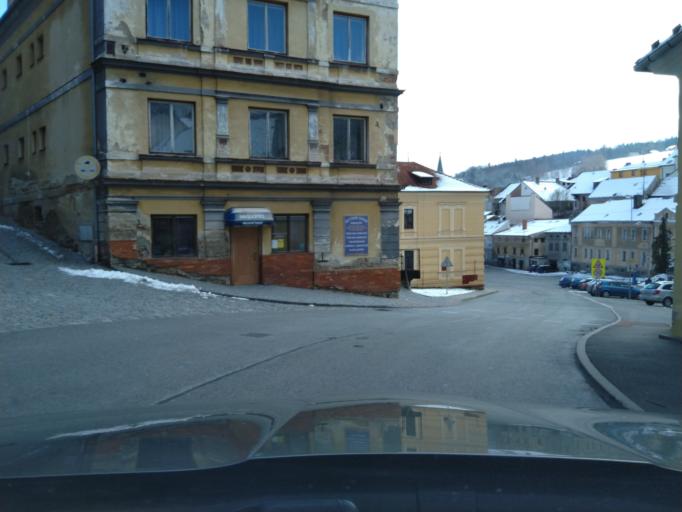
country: CZ
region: Jihocesky
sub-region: Okres Prachatice
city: Vimperk
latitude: 49.0537
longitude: 13.7715
